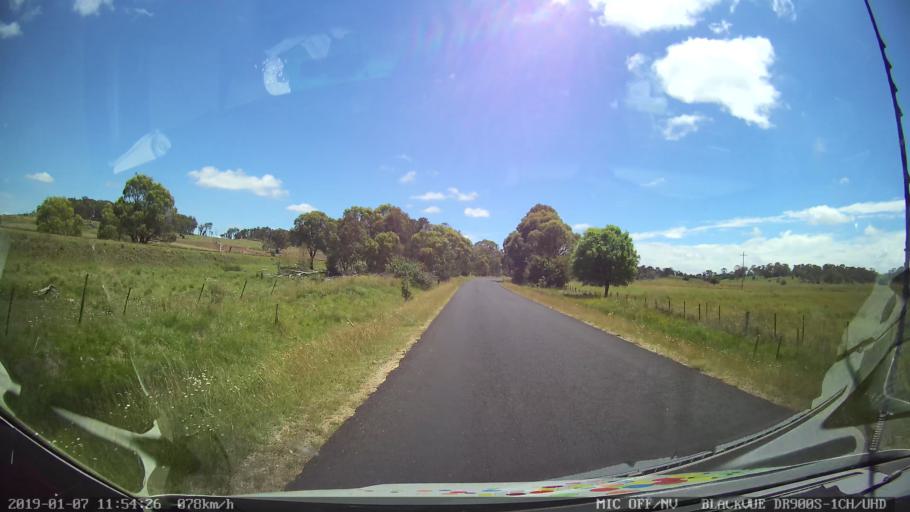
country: AU
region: New South Wales
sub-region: Guyra
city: Guyra
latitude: -30.2962
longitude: 151.6646
